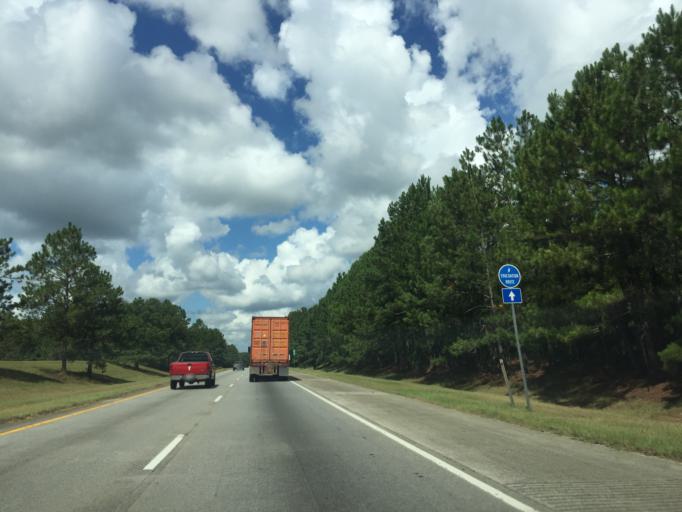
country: US
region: Georgia
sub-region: Candler County
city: Metter
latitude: 32.3834
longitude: -82.2329
